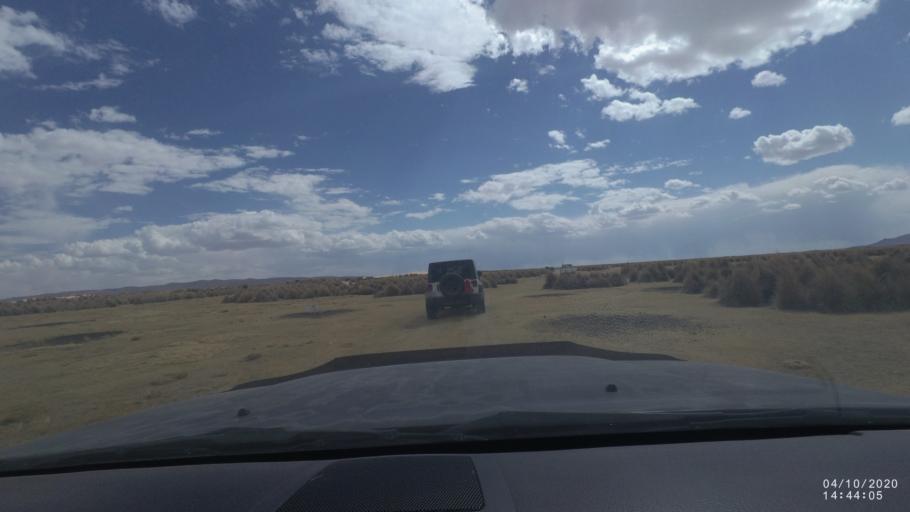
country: BO
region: Oruro
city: Poopo
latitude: -18.6865
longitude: -67.4947
